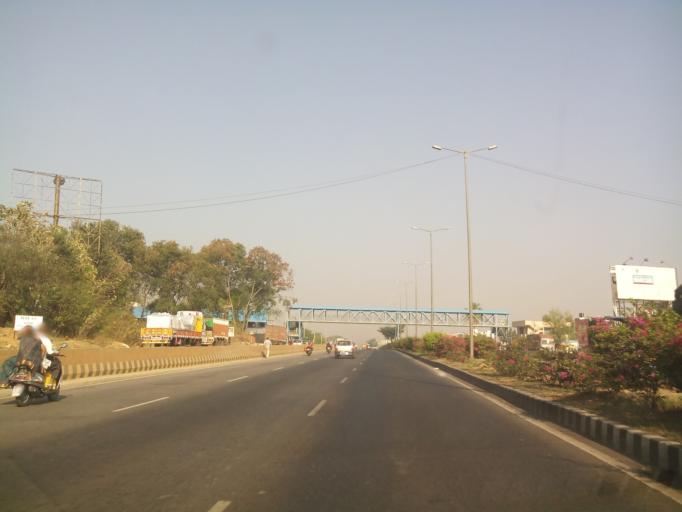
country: IN
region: Karnataka
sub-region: Bangalore Rural
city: Nelamangala
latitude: 13.0849
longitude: 77.4133
